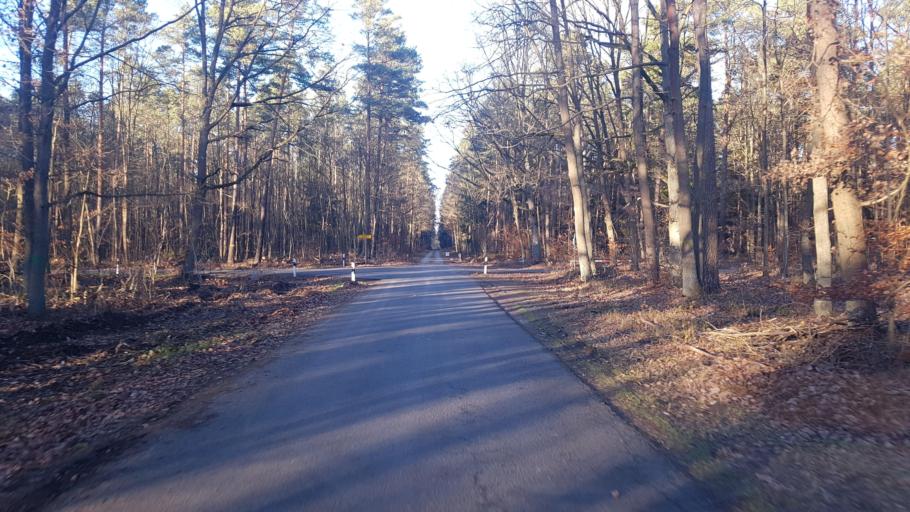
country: DE
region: Brandenburg
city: Tauer
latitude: 51.9364
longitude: 14.4779
